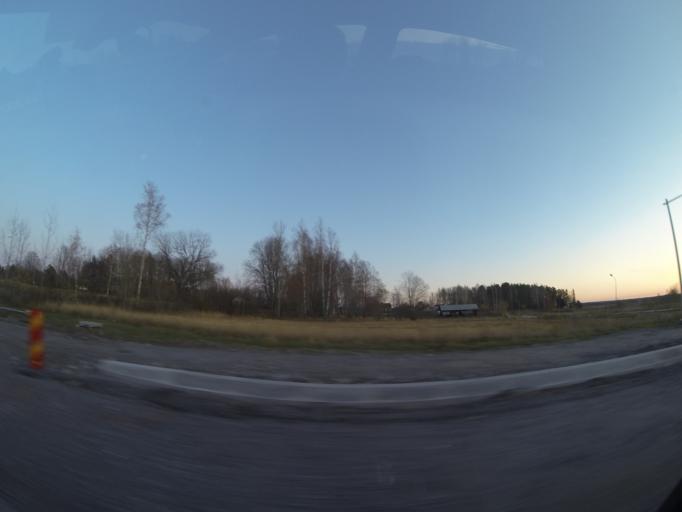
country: SE
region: OErebro
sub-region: Lindesbergs Kommun
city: Frovi
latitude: 59.3180
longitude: 15.3883
